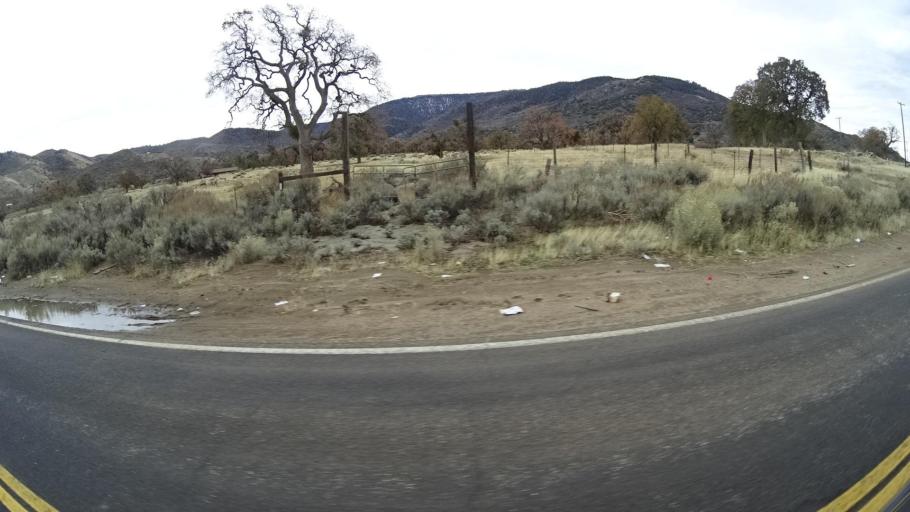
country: US
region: California
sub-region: Kern County
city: Stallion Springs
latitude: 35.0947
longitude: -118.5743
